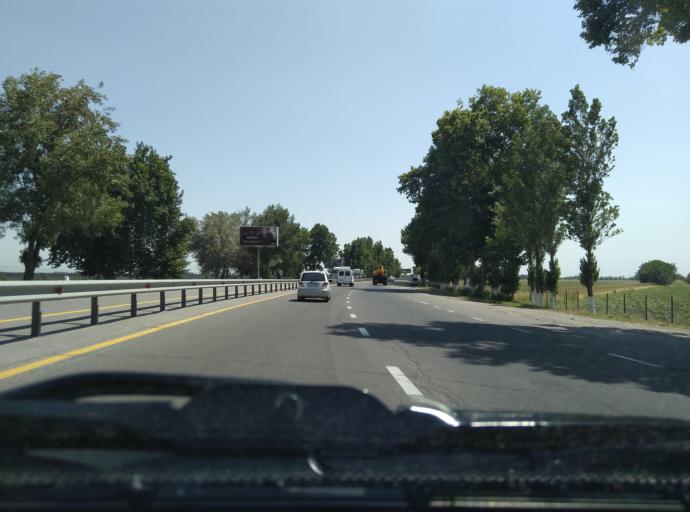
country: UZ
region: Toshkent Shahri
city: Bektemir
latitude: 41.2397
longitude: 69.4015
